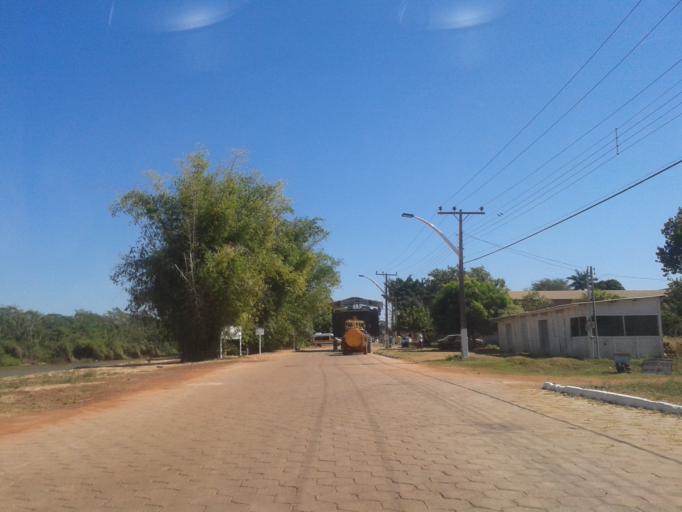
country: BR
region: Goias
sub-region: Sao Miguel Do Araguaia
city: Sao Miguel do Araguaia
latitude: -13.2180
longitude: -50.5766
